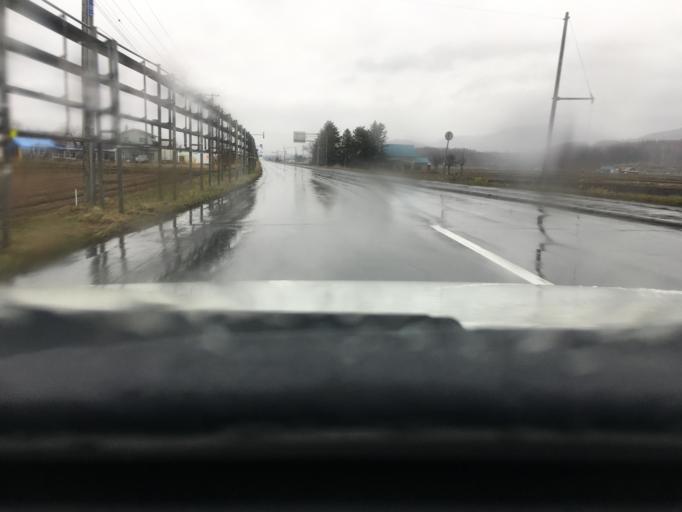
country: JP
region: Hokkaido
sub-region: Asahikawa-shi
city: Asahikawa
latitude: 43.8993
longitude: 142.5121
